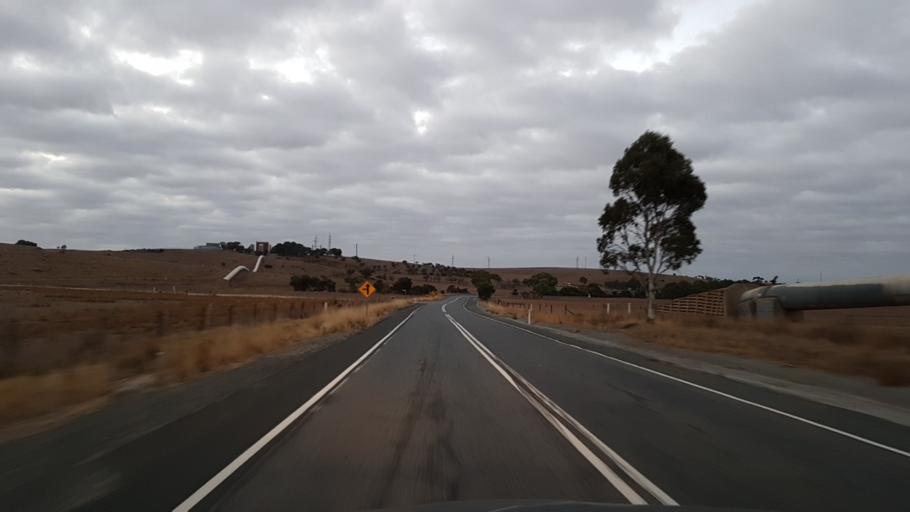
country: AU
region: South Australia
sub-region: Mount Barker
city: Callington
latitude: -35.0532
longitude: 139.0076
